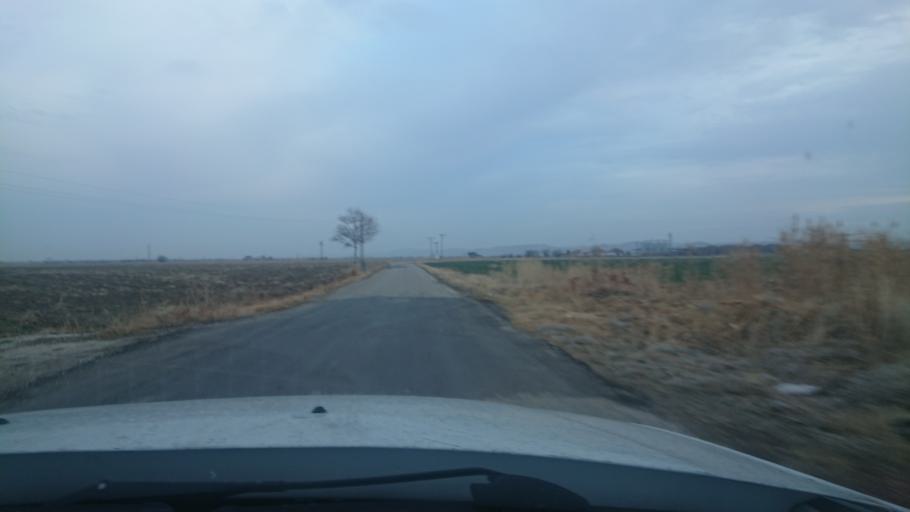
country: TR
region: Aksaray
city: Yesilova
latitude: 38.4478
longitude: 33.8351
